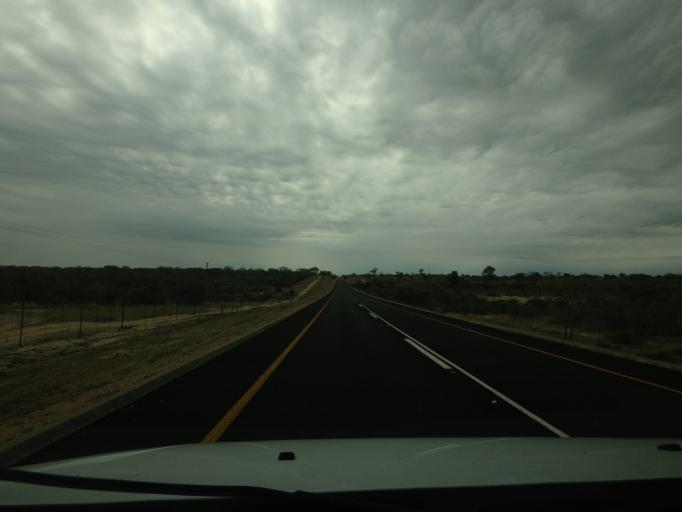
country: ZA
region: Limpopo
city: Thulamahashi
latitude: -24.5638
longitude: 31.1328
